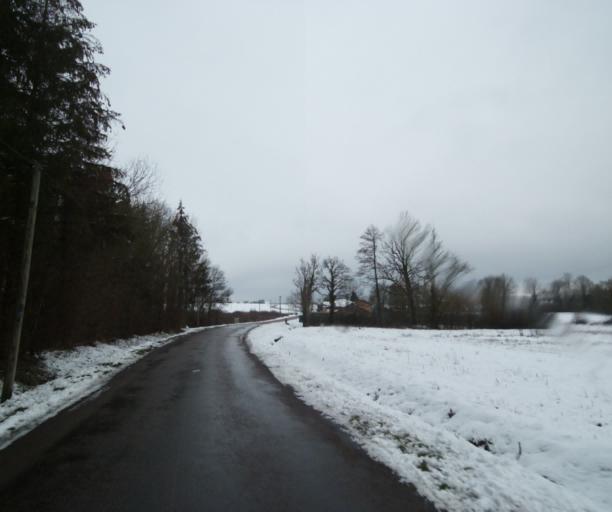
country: FR
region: Champagne-Ardenne
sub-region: Departement de la Haute-Marne
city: Laneuville-a-Remy
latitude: 48.5116
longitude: 4.8470
